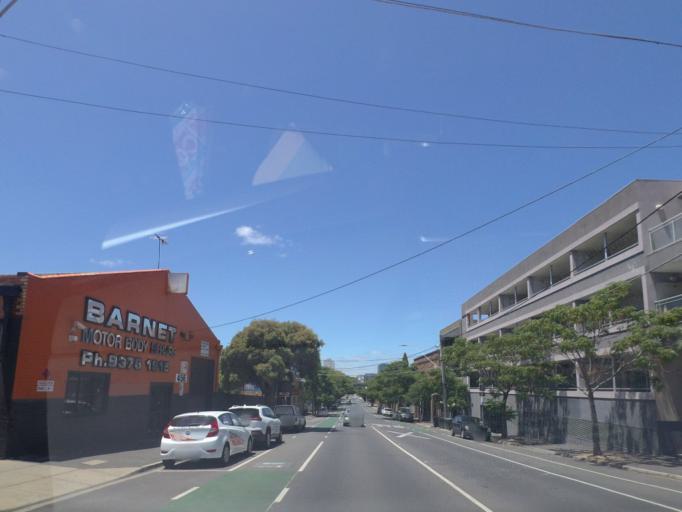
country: AU
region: Victoria
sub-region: Moonee Valley
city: Flemington
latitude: -37.7946
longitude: 144.9313
